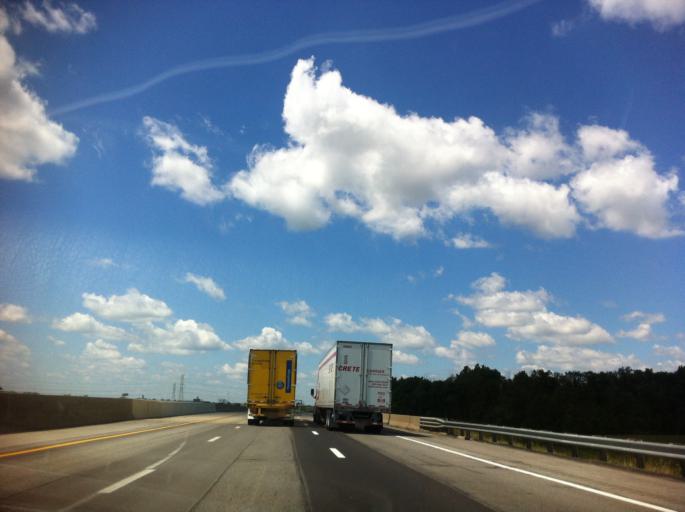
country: US
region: Ohio
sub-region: Wood County
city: Millbury
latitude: 41.5152
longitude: -83.4347
